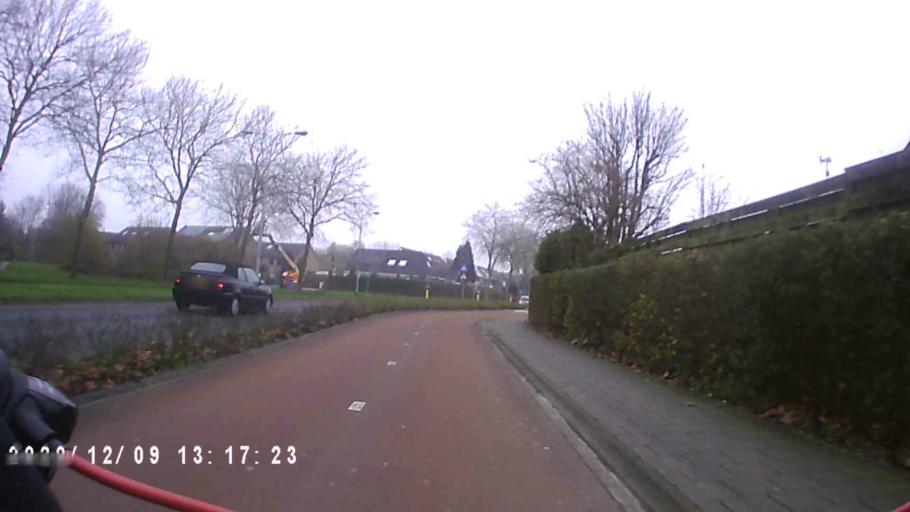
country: NL
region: Groningen
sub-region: Gemeente Groningen
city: Korrewegwijk
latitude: 53.2518
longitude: 6.5880
